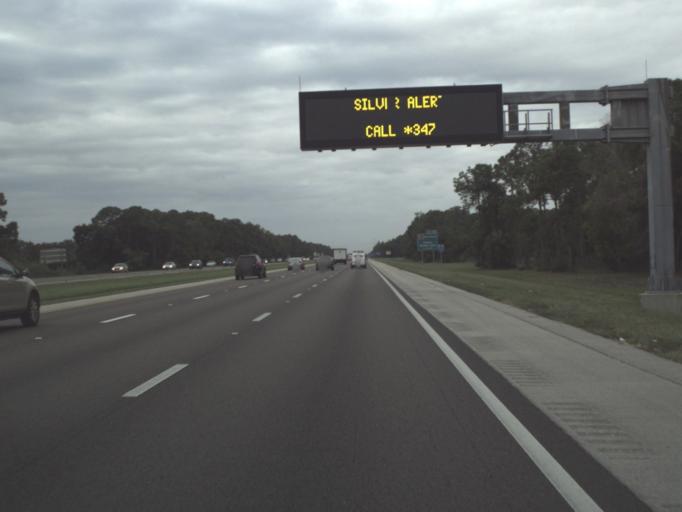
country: US
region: Florida
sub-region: Collier County
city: Vineyards
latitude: 26.2367
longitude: -81.7368
